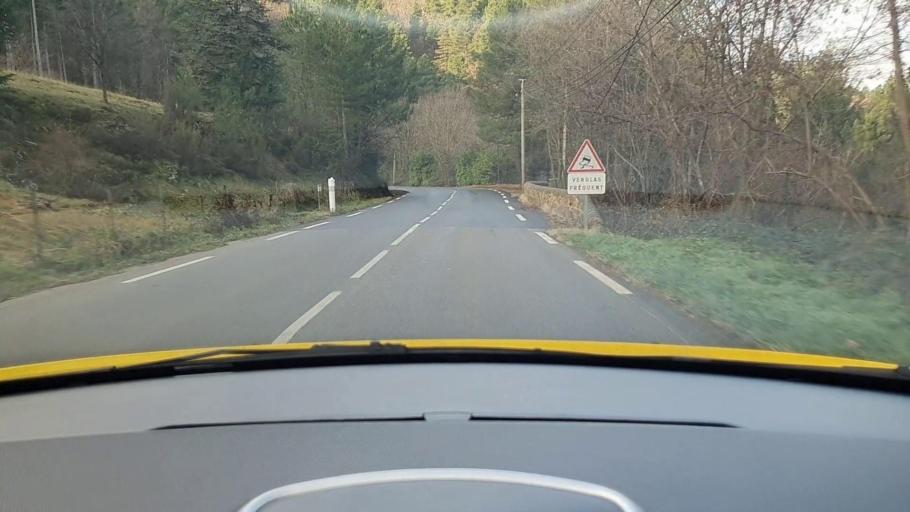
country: FR
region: Languedoc-Roussillon
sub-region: Departement du Gard
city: Branoux-les-Taillades
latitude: 44.2789
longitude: 4.0002
